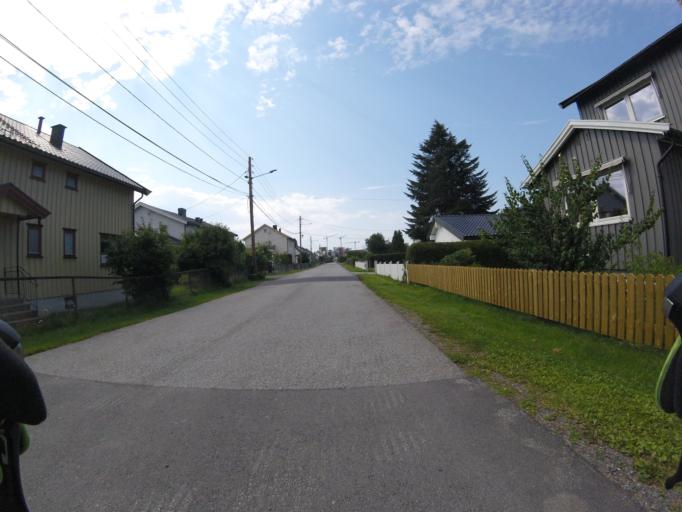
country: NO
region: Akershus
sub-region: Skedsmo
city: Lillestrom
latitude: 59.9579
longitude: 11.0680
